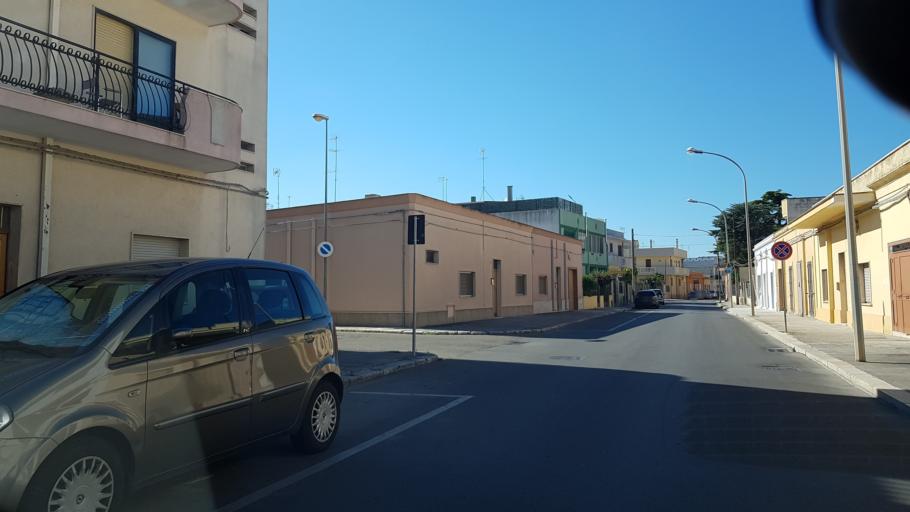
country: IT
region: Apulia
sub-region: Provincia di Brindisi
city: Mesagne
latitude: 40.5521
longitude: 17.8109
